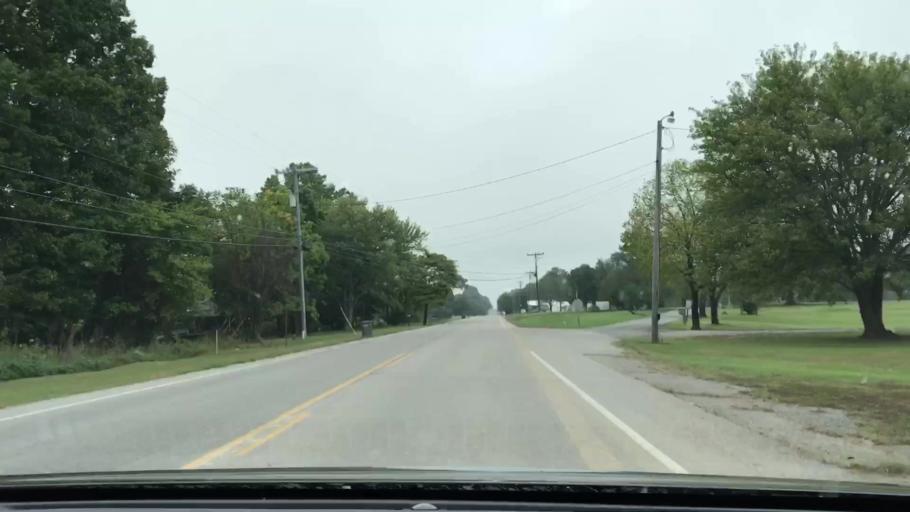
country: US
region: Tennessee
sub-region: Sumner County
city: Portland
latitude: 36.4996
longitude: -86.4979
